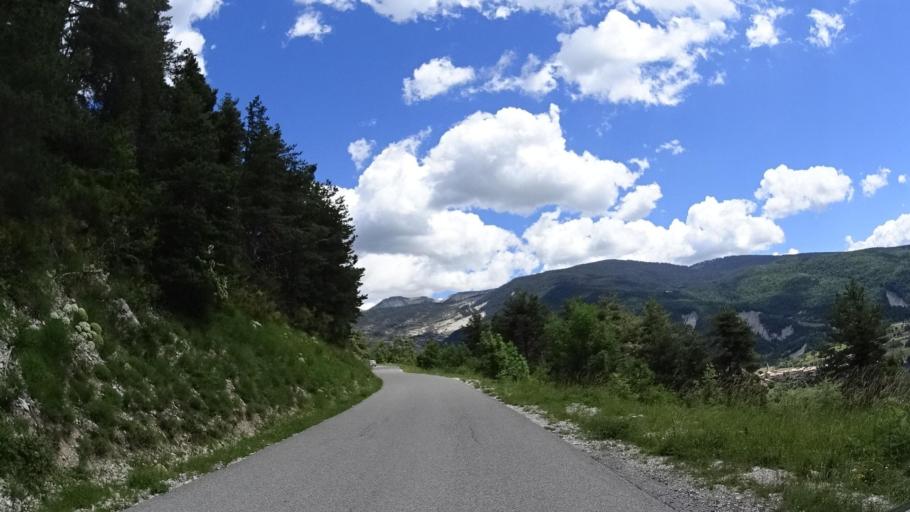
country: FR
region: Provence-Alpes-Cote d'Azur
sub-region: Departement des Alpes-de-Haute-Provence
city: Annot
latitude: 44.0210
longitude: 6.6189
